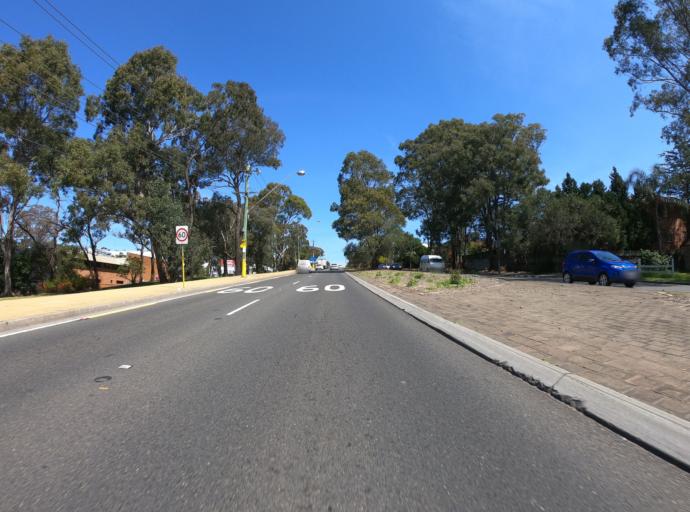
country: AU
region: New South Wales
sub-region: The Hills Shire
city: Castle Hill
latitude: -33.7240
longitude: 150.9801
